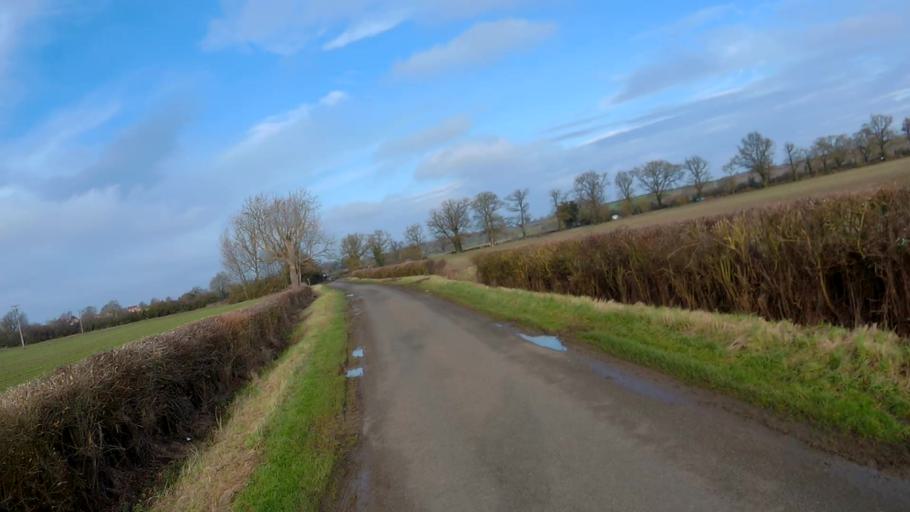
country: GB
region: England
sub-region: Lincolnshire
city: Bourne
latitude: 52.7749
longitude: -0.4262
